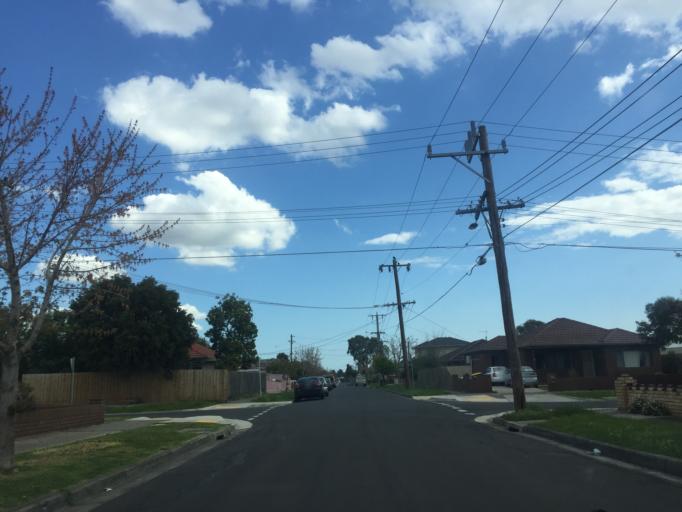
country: AU
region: Victoria
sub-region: Darebin
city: Kingsbury
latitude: -37.7145
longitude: 145.0416
